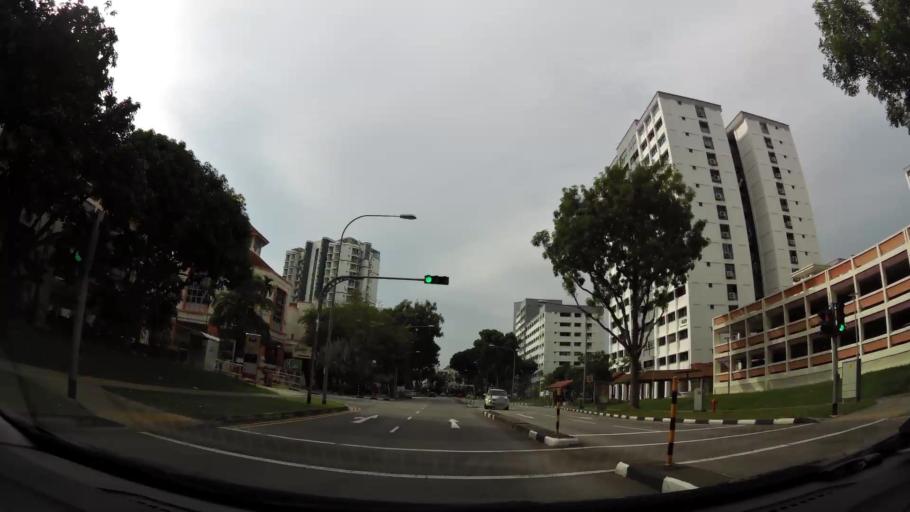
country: MY
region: Johor
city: Kampung Pasir Gudang Baru
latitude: 1.3793
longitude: 103.8889
